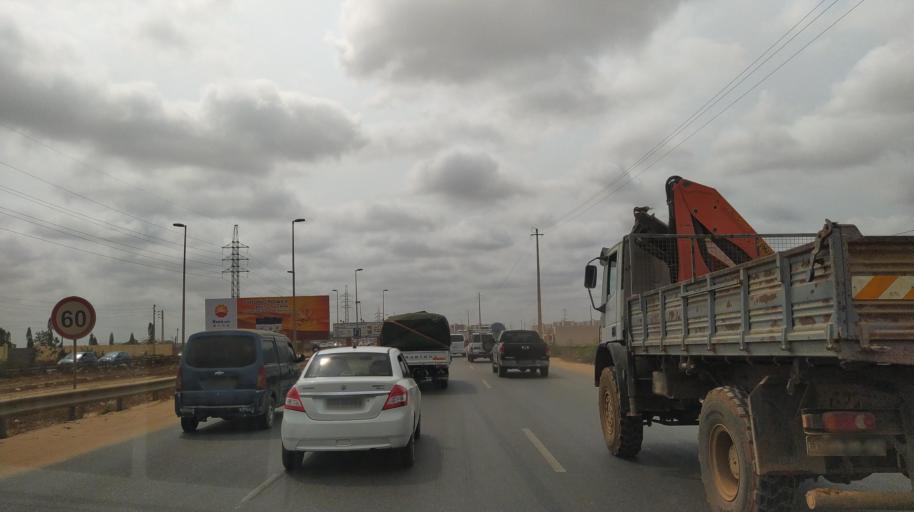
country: AO
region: Luanda
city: Luanda
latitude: -8.9770
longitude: 13.3821
